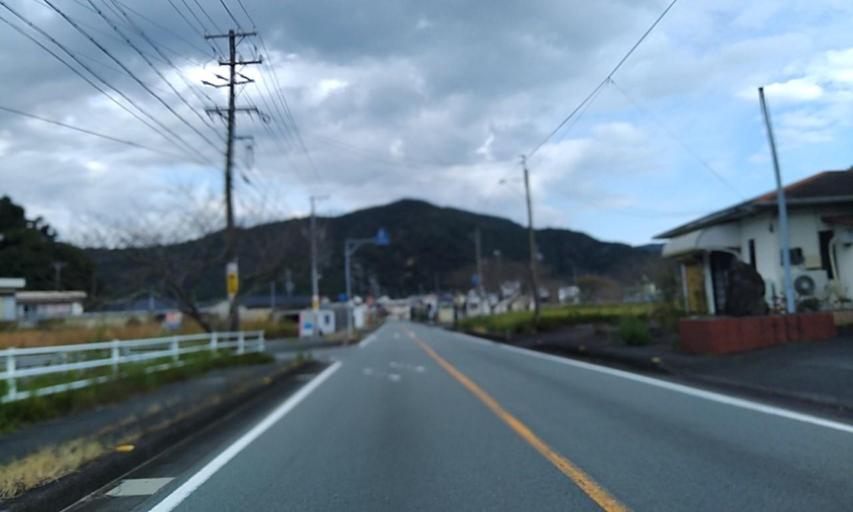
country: JP
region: Mie
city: Ise
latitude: 34.2780
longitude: 136.4944
